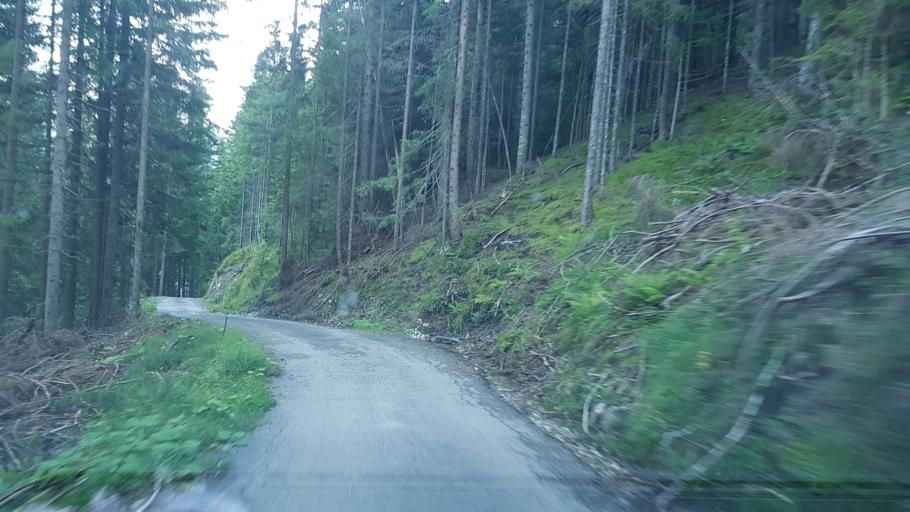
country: IT
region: Veneto
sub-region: Provincia di Belluno
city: San Pietro di Cadore
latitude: 46.5974
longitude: 12.5916
